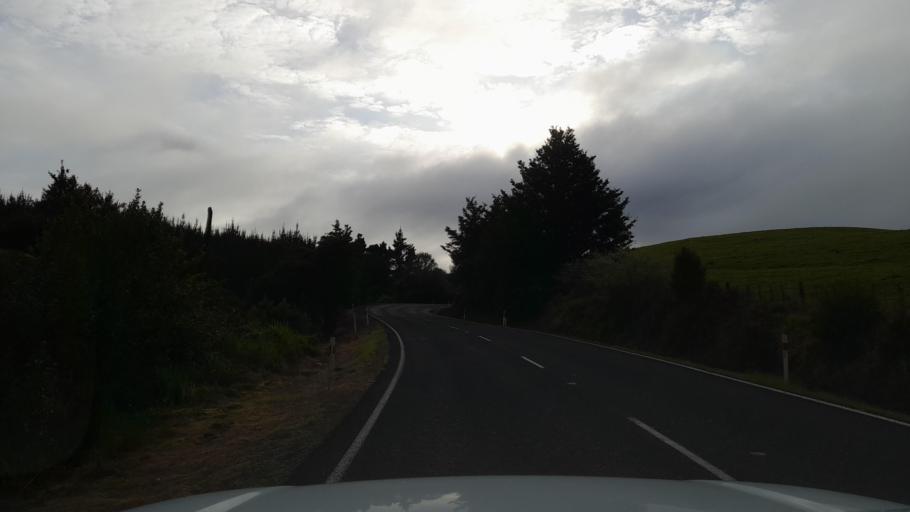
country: NZ
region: Northland
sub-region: Far North District
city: Waimate North
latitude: -35.5133
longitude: 173.8348
